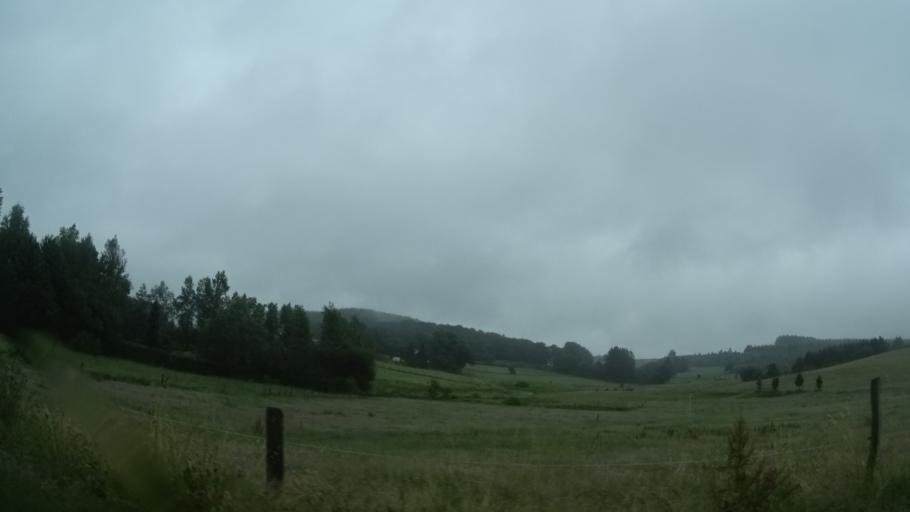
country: BE
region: Wallonia
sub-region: Province du Luxembourg
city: Leglise
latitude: 49.7991
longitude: 5.5394
